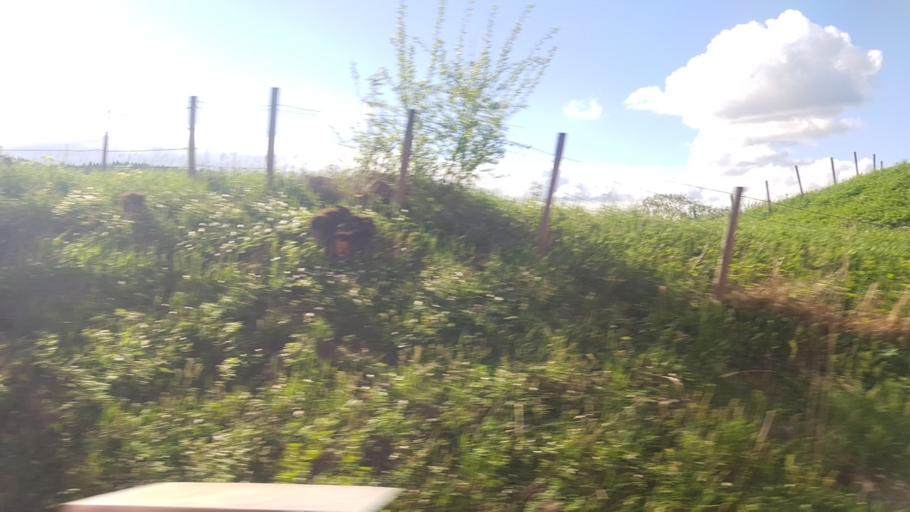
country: NO
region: Sor-Trondelag
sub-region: Midtre Gauldal
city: Storen
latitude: 62.9743
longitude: 10.2134
